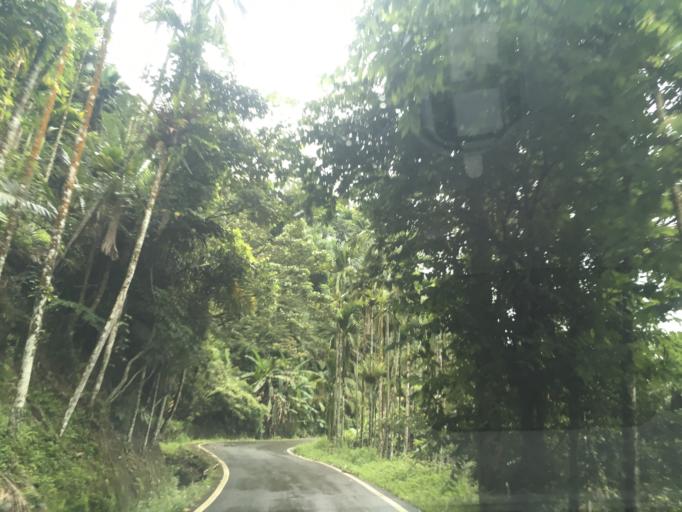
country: TW
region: Taiwan
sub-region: Yunlin
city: Douliu
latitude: 23.5642
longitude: 120.6454
